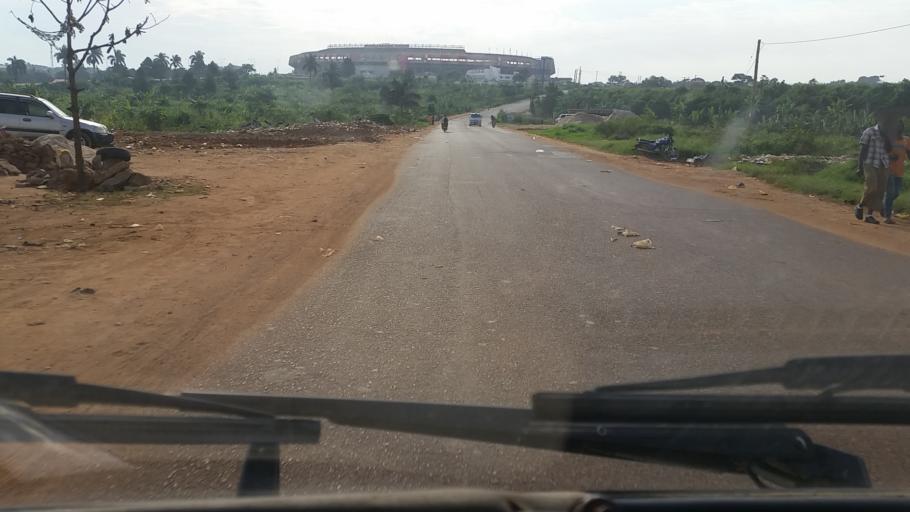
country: UG
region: Central Region
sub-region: Wakiso District
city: Kireka
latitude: 0.3458
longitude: 32.6523
